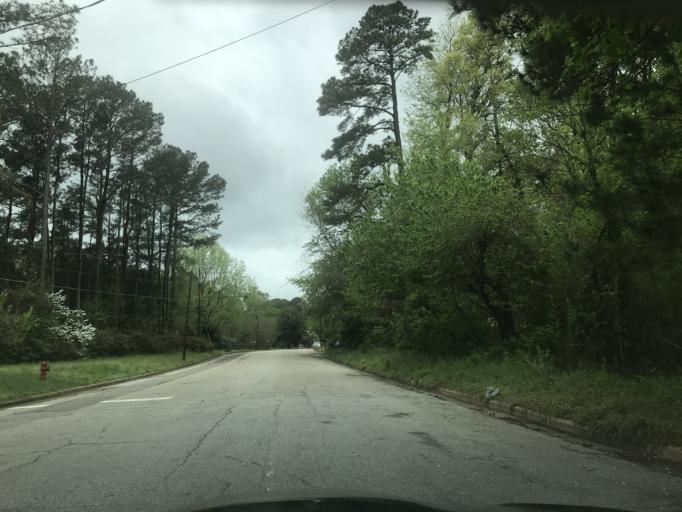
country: US
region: North Carolina
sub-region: Wake County
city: Raleigh
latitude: 35.7490
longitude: -78.6507
